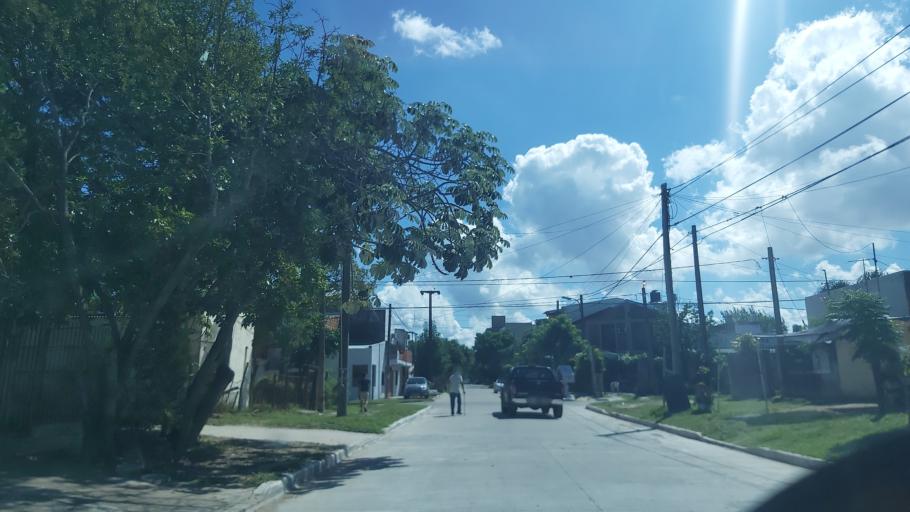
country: AR
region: Corrientes
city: Corrientes
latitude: -27.4781
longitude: -58.8500
